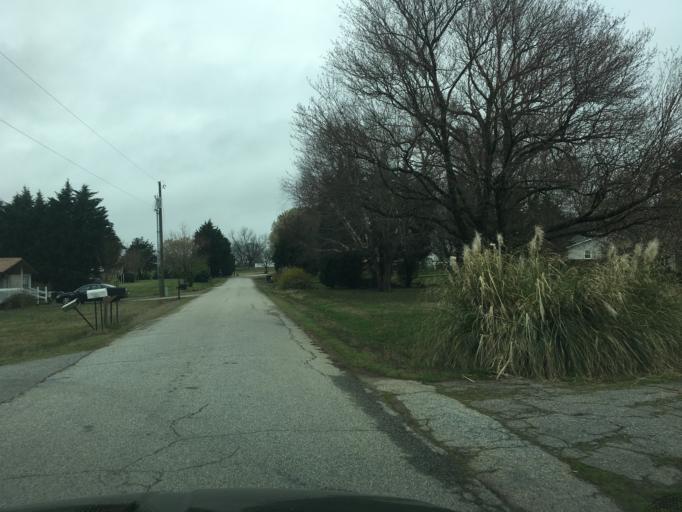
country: US
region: South Carolina
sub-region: Spartanburg County
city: Inman Mills
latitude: 35.0277
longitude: -82.1170
